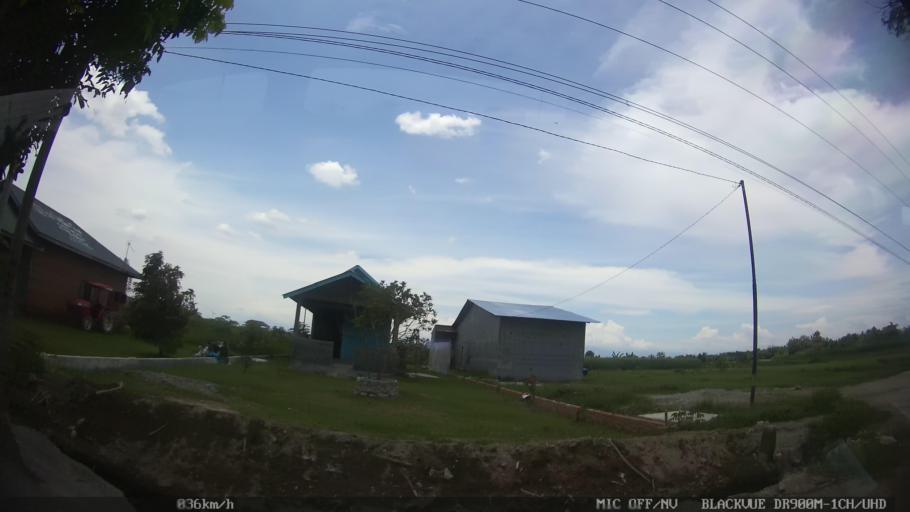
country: ID
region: North Sumatra
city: Binjai
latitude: 3.5910
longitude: 98.5097
